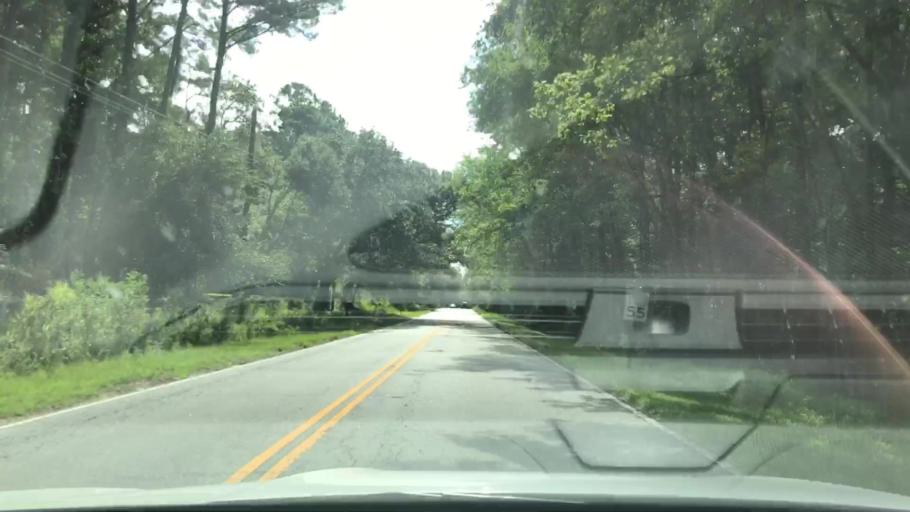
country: US
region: South Carolina
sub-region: Dorchester County
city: Centerville
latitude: 32.9462
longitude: -80.1998
